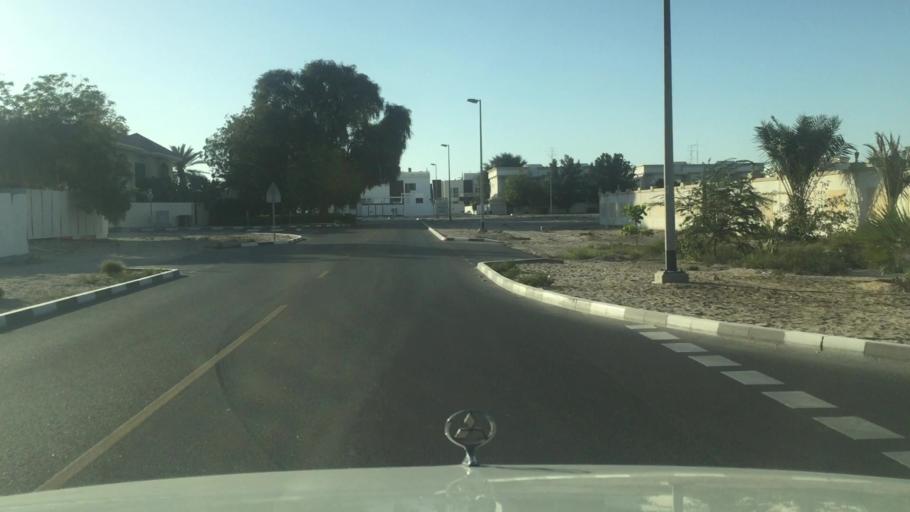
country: AE
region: Dubai
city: Dubai
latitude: 25.1624
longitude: 55.2280
